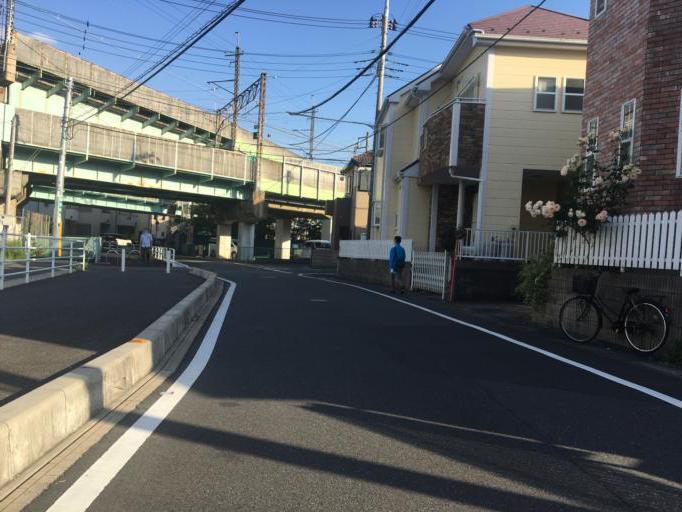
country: JP
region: Saitama
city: Yono
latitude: 35.8523
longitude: 139.6359
